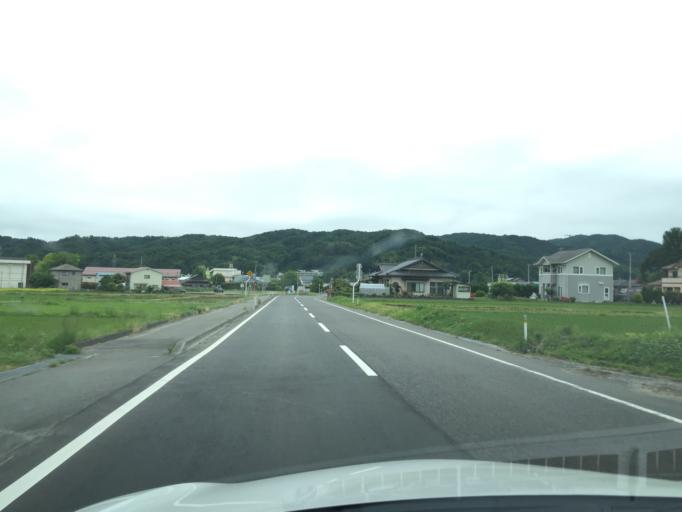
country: JP
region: Fukushima
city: Funehikimachi-funehiki
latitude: 37.3262
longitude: 140.6667
